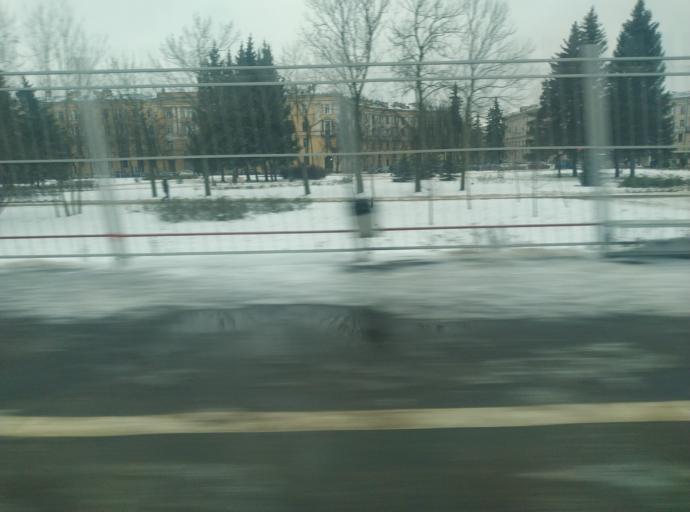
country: RU
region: St.-Petersburg
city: Kolpino
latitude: 59.7495
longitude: 30.6150
